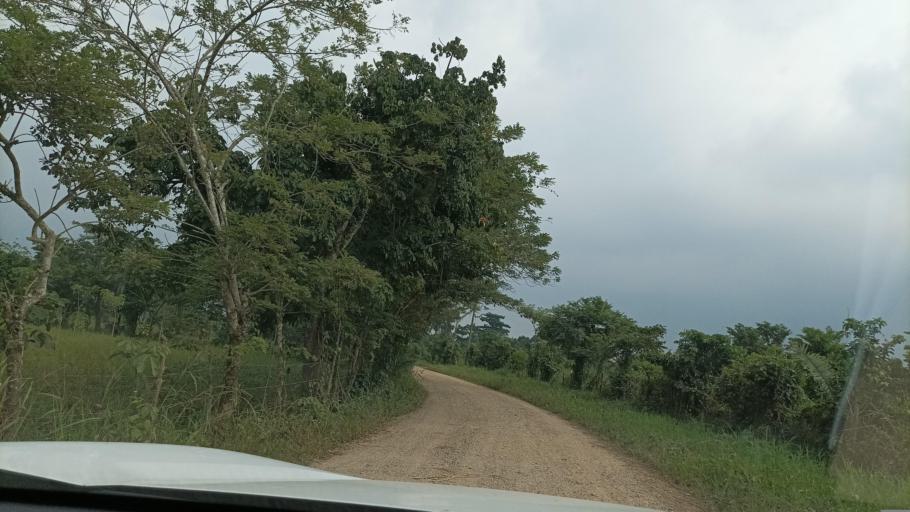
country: MX
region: Veracruz
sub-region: Moloacan
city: Cuichapa
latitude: 17.5821
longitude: -94.2104
